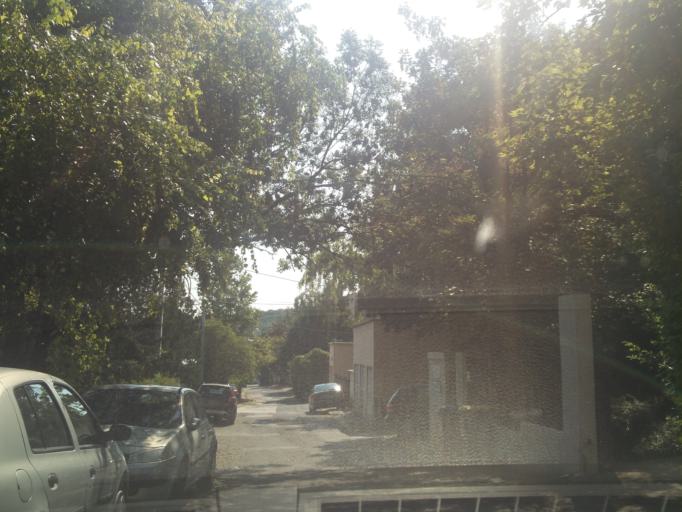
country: HU
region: Budapest
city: Budapest XII. keruelet
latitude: 47.5079
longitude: 18.9991
